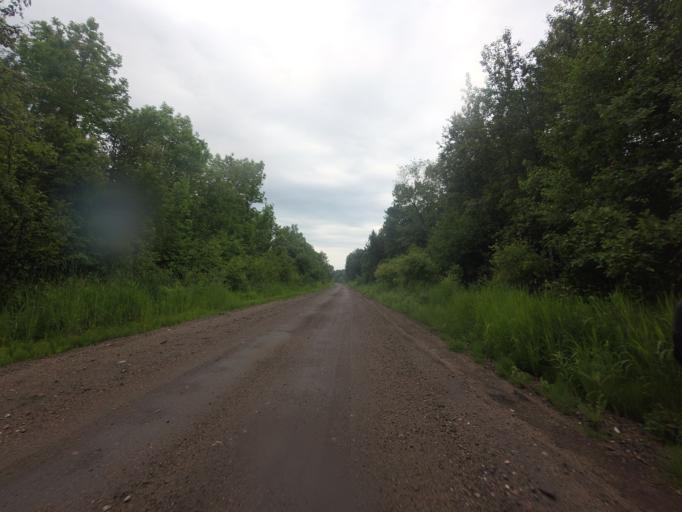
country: CA
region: Quebec
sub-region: Outaouais
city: Maniwaki
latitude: 46.3445
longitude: -75.9997
